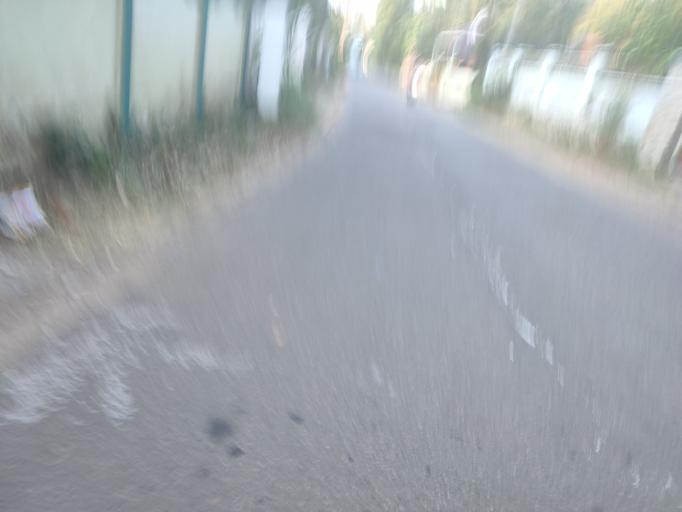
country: IN
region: Kerala
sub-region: Thrissur District
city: Kizhake Chalakudi
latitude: 10.2289
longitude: 76.3291
